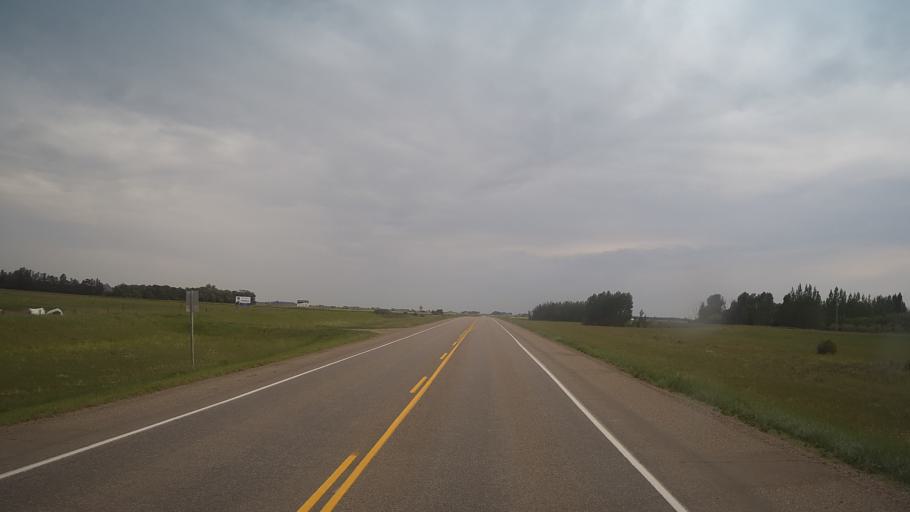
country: CA
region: Saskatchewan
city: Langham
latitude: 52.1288
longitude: -107.2345
